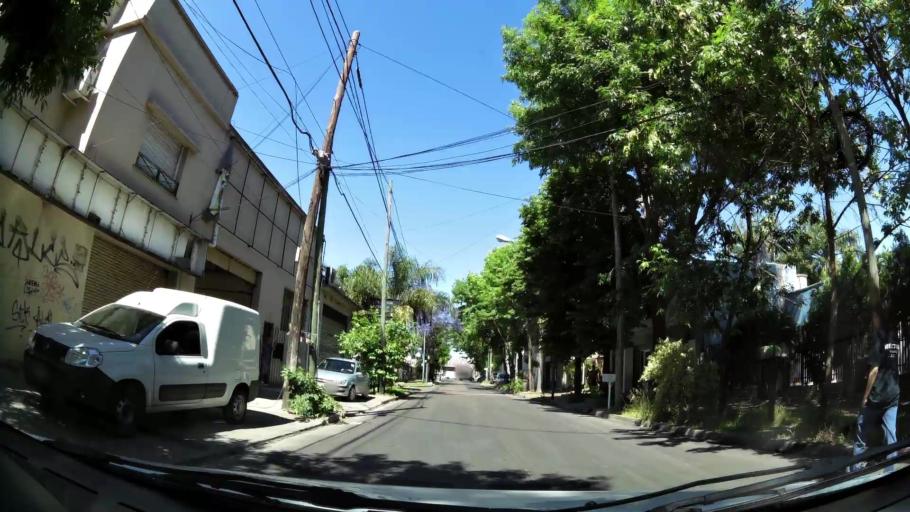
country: AR
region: Buenos Aires
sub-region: Partido de General San Martin
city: General San Martin
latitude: -34.5384
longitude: -58.5427
